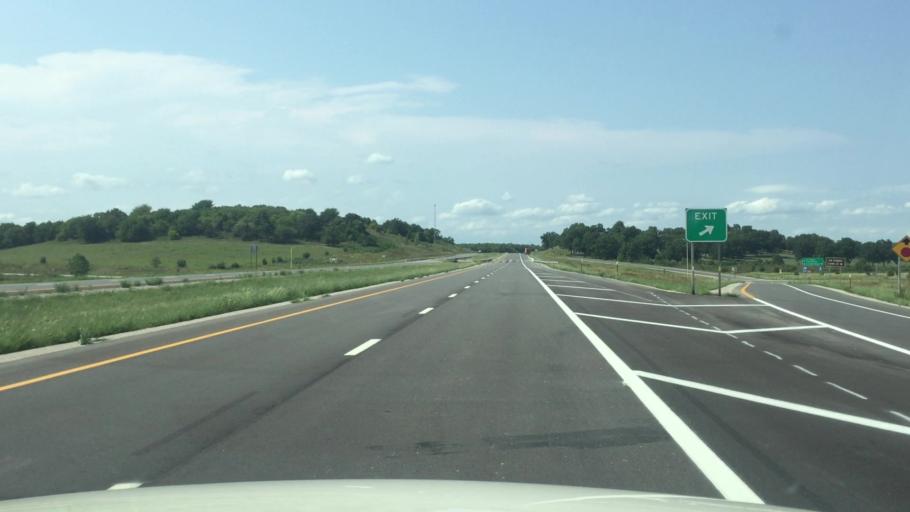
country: US
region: Kansas
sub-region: Linn County
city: La Cygne
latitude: 38.3428
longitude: -94.6815
